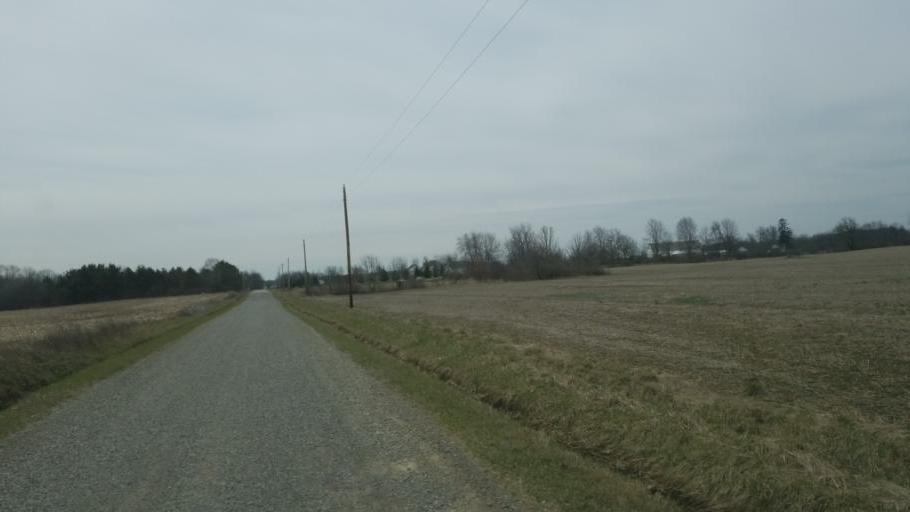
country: US
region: Ohio
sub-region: Knox County
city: Centerburg
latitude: 40.3146
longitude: -82.6489
